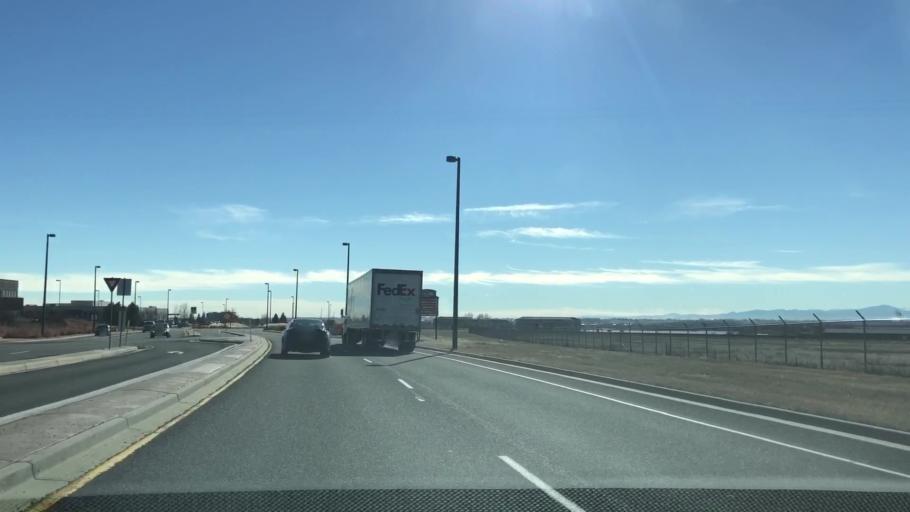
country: US
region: Colorado
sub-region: Larimer County
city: Loveland
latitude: 40.4278
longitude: -105.0001
